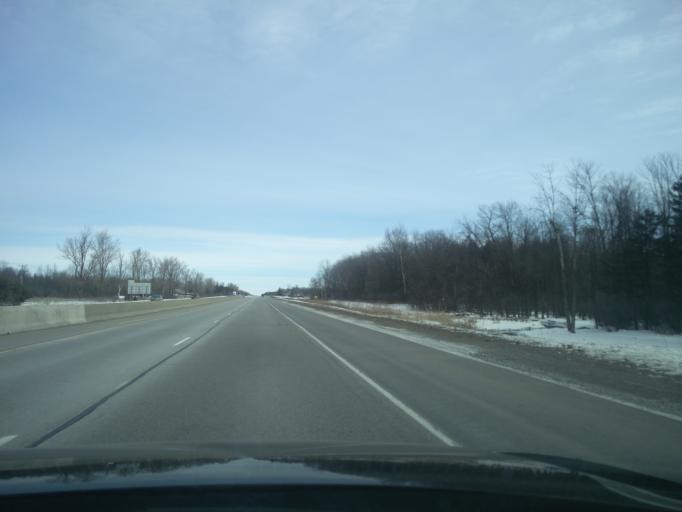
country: CA
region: Ontario
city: Brockville
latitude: 44.6579
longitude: -75.6199
